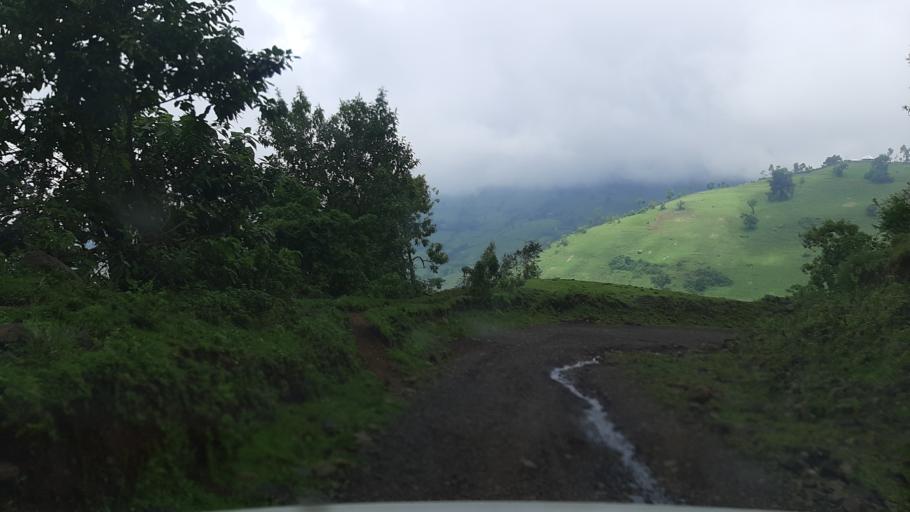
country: ET
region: Southern Nations, Nationalities, and People's Region
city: Bonga
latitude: 7.1423
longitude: 36.5715
